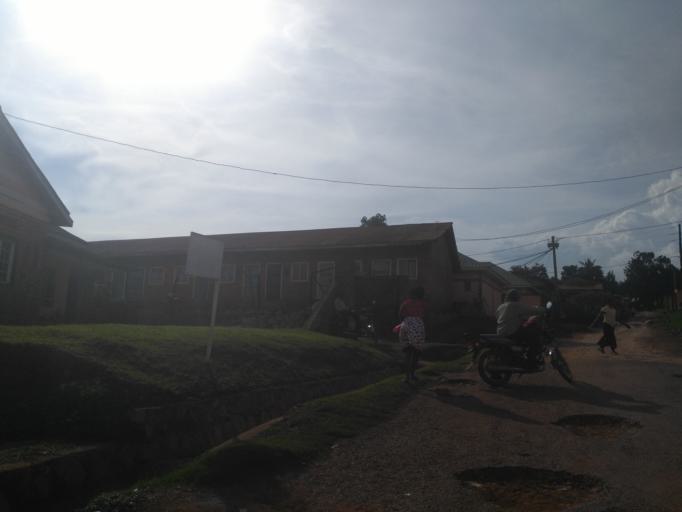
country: UG
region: Central Region
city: Kampala Central Division
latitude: 0.3606
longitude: 32.5699
